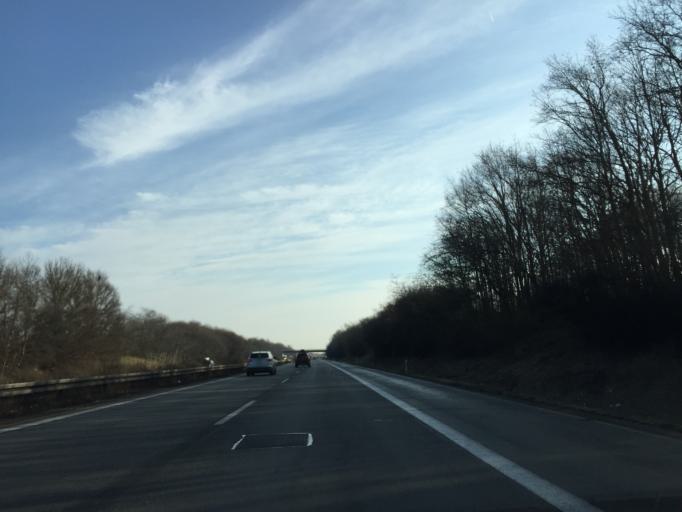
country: DE
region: Bavaria
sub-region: Regierungsbezirk Unterfranken
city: Mainstockheim
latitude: 49.7869
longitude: 10.1621
